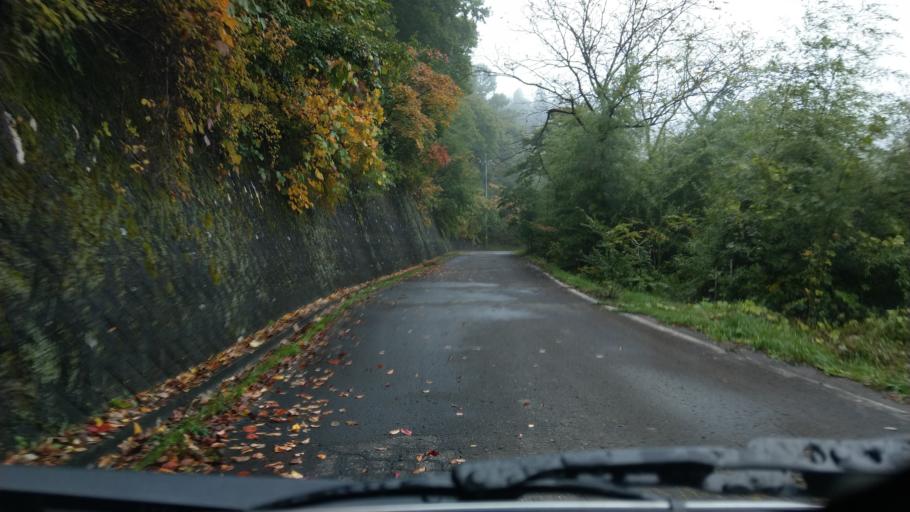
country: JP
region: Nagano
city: Komoro
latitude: 36.3632
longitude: 138.4465
